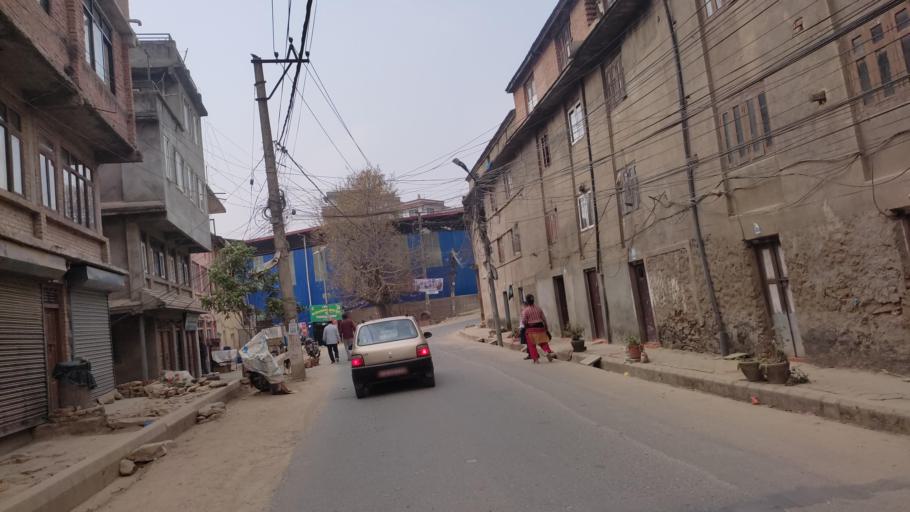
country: NP
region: Central Region
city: Kirtipur
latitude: 27.6817
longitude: 85.2724
